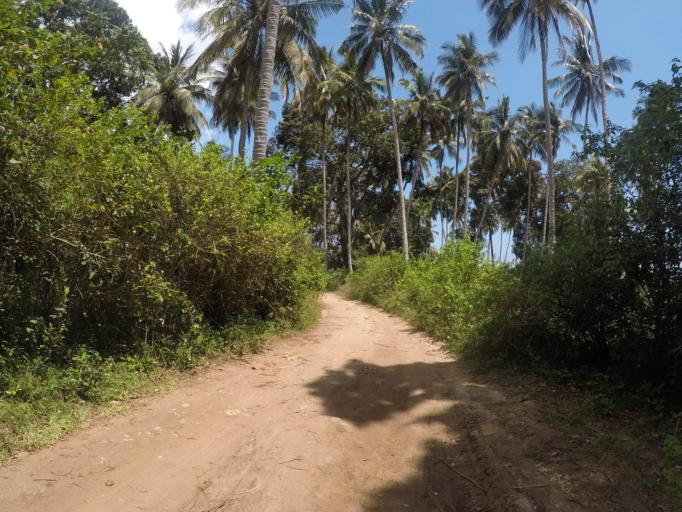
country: TZ
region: Zanzibar North
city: Mkokotoni
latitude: -5.9893
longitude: 39.1869
